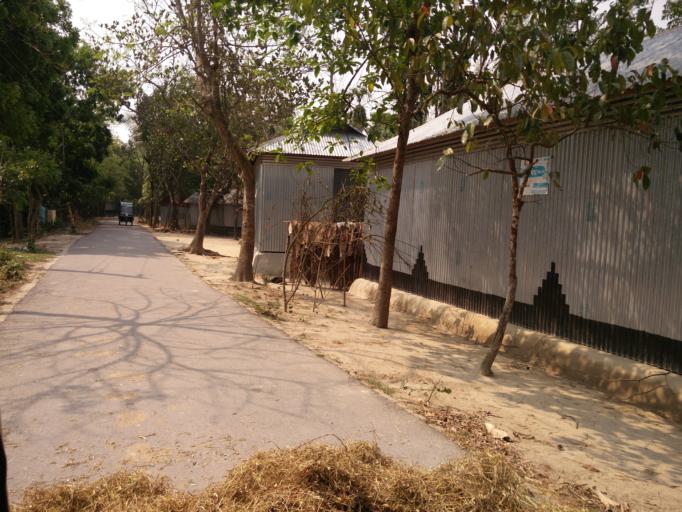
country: BD
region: Dhaka
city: Muktagacha
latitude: 24.9001
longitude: 90.2592
